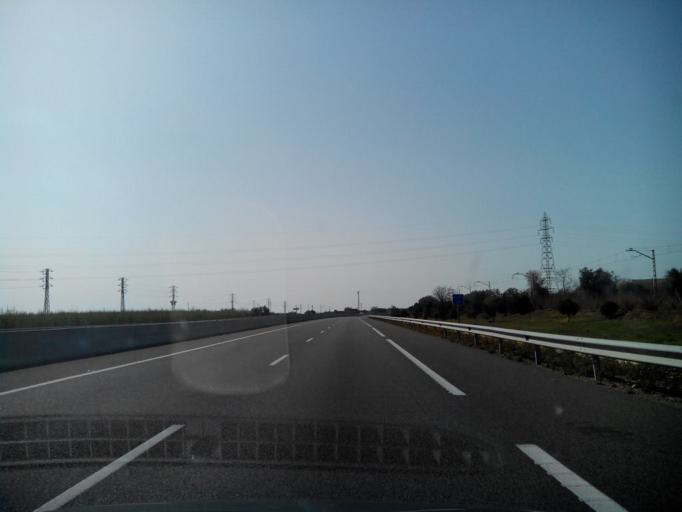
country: ES
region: Catalonia
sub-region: Provincia de Tarragona
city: La Selva
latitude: 41.2303
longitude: 1.1622
